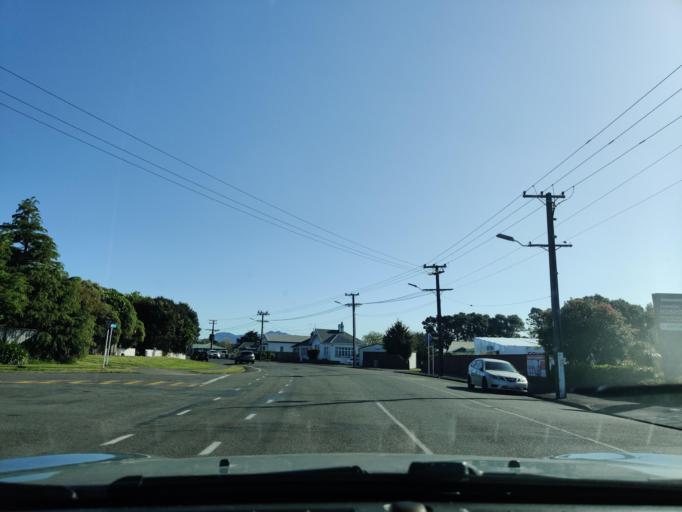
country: NZ
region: Taranaki
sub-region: New Plymouth District
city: New Plymouth
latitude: -39.0748
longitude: 174.0577
